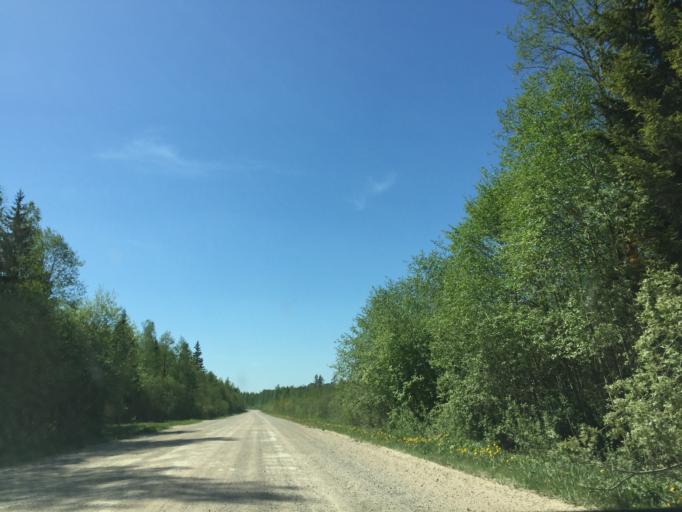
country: LV
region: Kegums
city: Kegums
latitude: 56.8822
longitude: 24.7852
